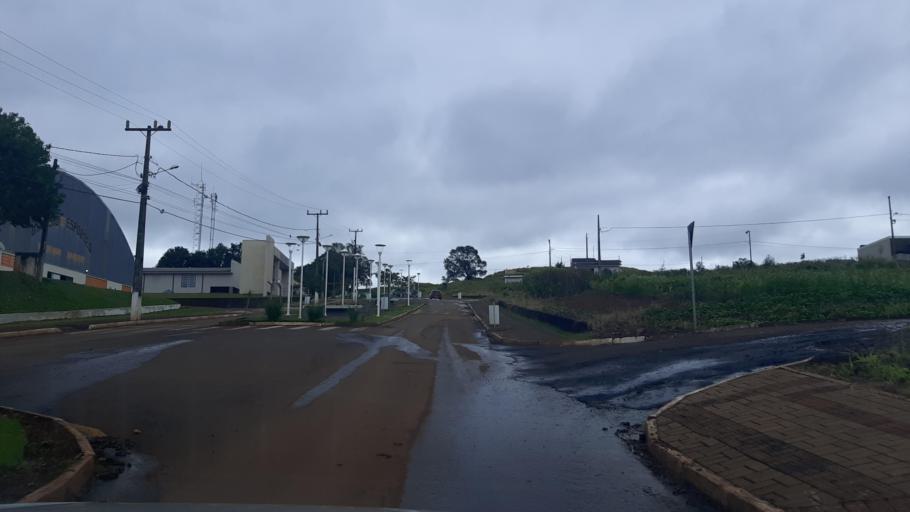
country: BR
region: Parana
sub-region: Ampere
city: Ampere
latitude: -26.0350
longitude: -53.4862
